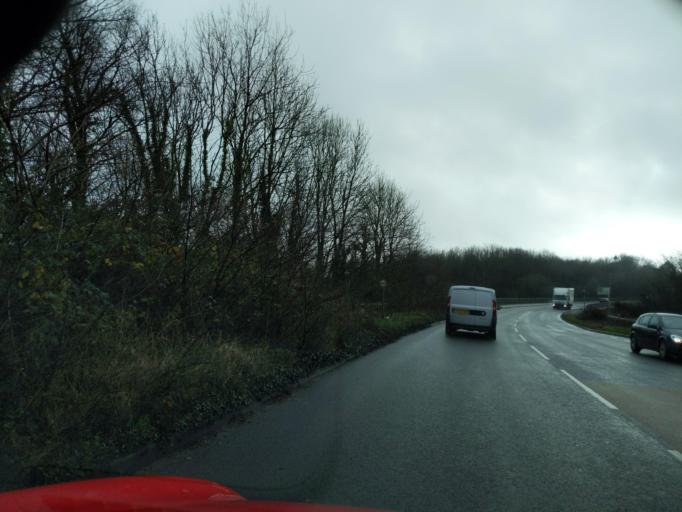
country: GB
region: England
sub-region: Devon
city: Plympton
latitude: 50.3800
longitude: -4.0240
